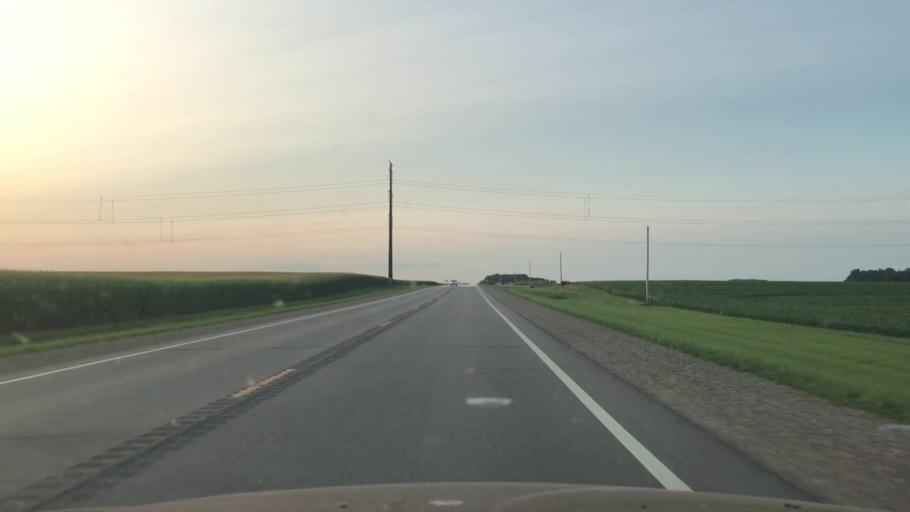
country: US
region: Minnesota
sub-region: Redwood County
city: Redwood Falls
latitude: 44.4318
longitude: -95.1176
